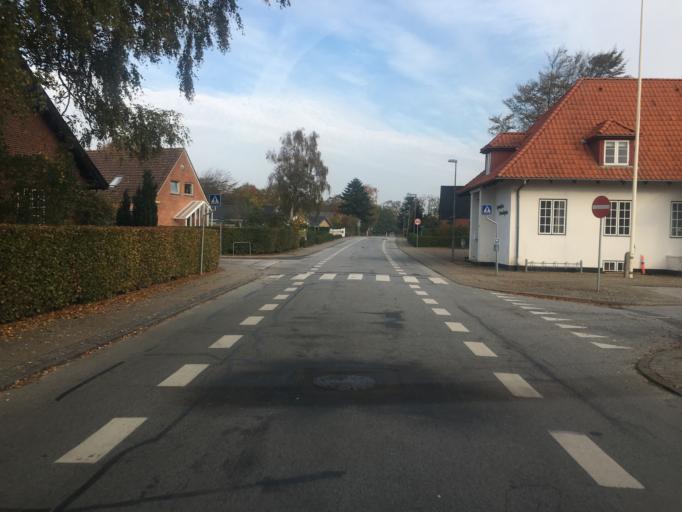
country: DK
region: South Denmark
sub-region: Tonder Kommune
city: Logumkloster
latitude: 55.0606
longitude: 8.9552
